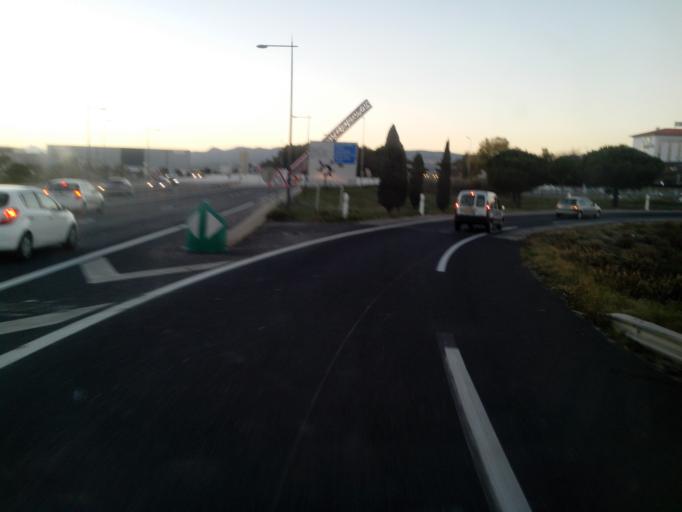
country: FR
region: Languedoc-Roussillon
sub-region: Departement des Pyrenees-Orientales
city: Rivesaltes
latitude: 42.7798
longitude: 2.9011
